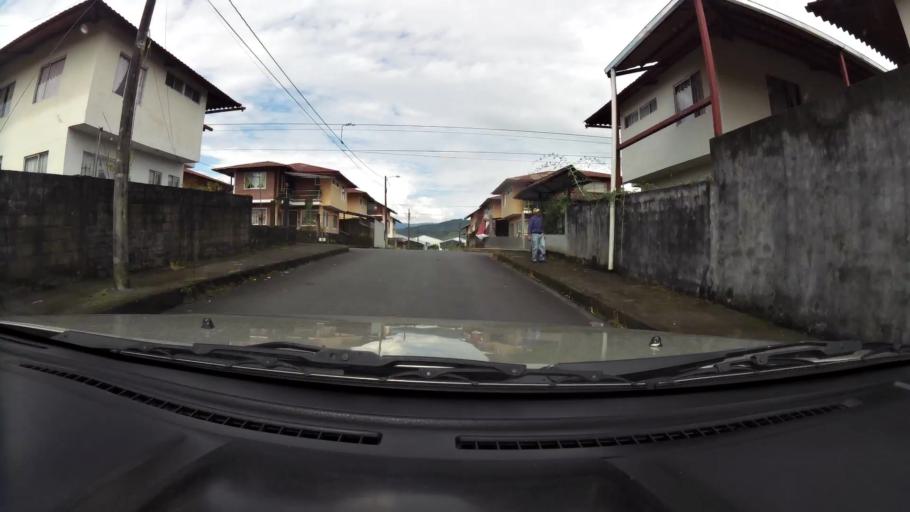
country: EC
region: Pastaza
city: Puyo
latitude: -1.5018
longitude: -78.0000
